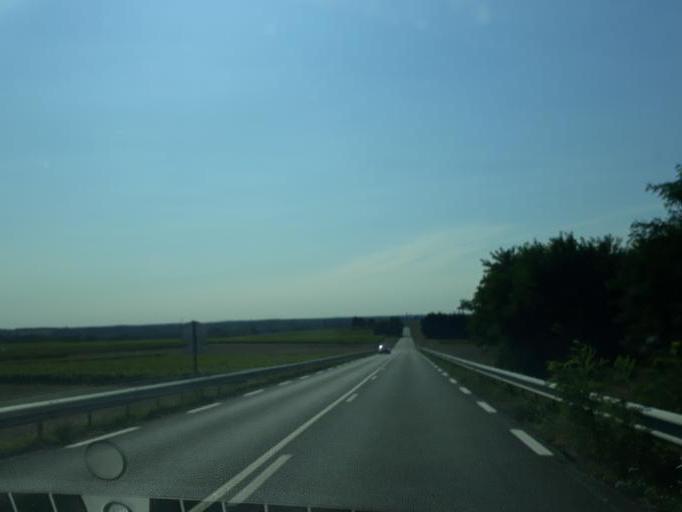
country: FR
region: Centre
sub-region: Departement du Loir-et-Cher
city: Noyers-sur-Cher
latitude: 47.2743
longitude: 1.4440
